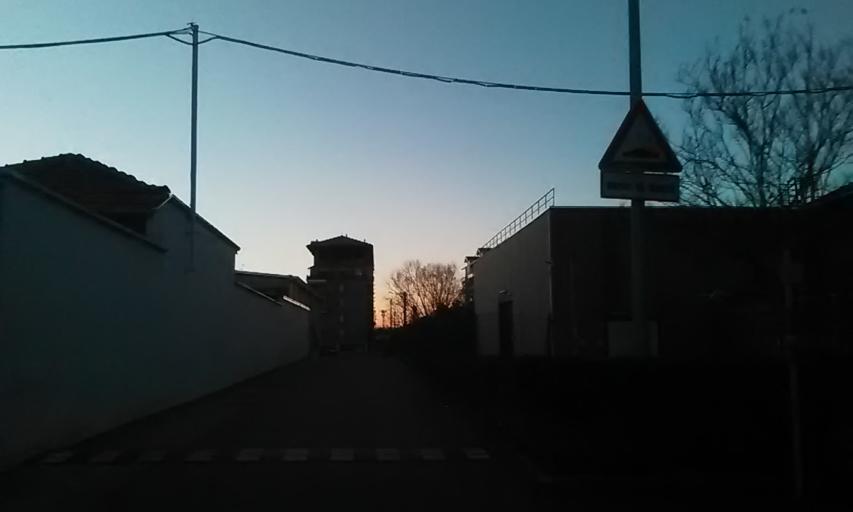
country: IT
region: Piedmont
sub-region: Provincia di Biella
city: Biella
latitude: 45.5582
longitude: 8.0445
